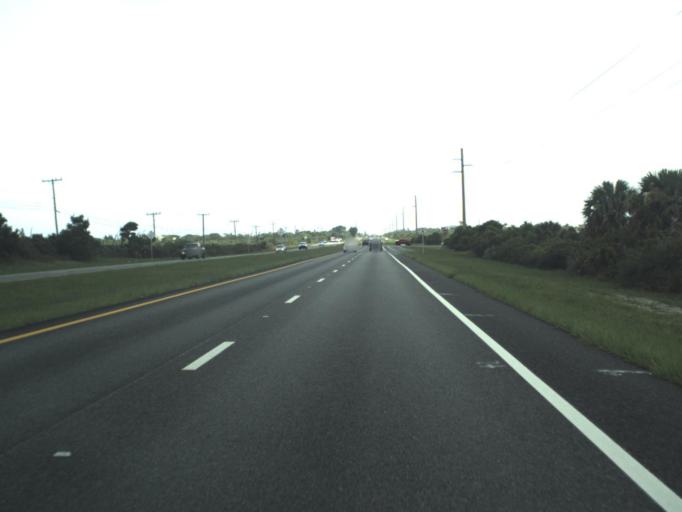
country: US
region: Florida
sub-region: Palm Beach County
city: Tequesta
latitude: 27.0063
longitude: -80.1014
